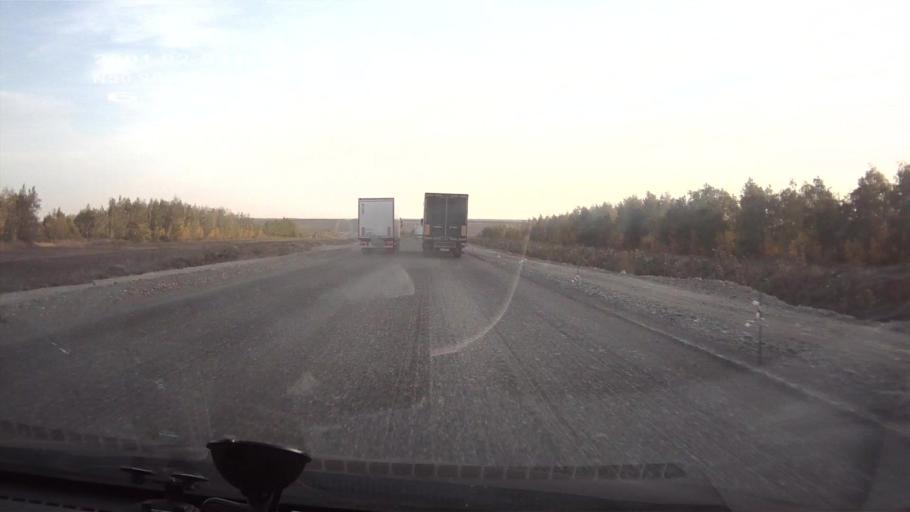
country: RU
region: Saratov
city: Krasnoarmeysk
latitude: 50.9967
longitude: 45.6127
